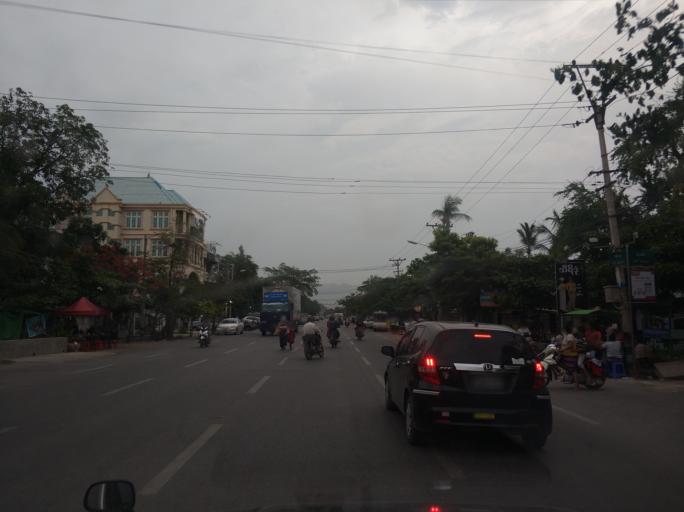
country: MM
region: Mandalay
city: Mandalay
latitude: 21.9756
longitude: 96.1095
